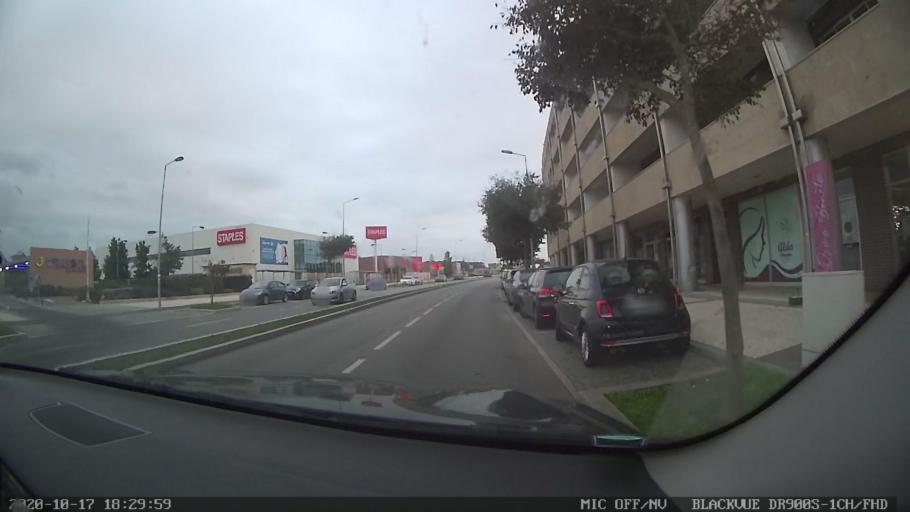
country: PT
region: Porto
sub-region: Vila do Conde
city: Vila do Conde
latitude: 41.3703
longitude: -8.7444
